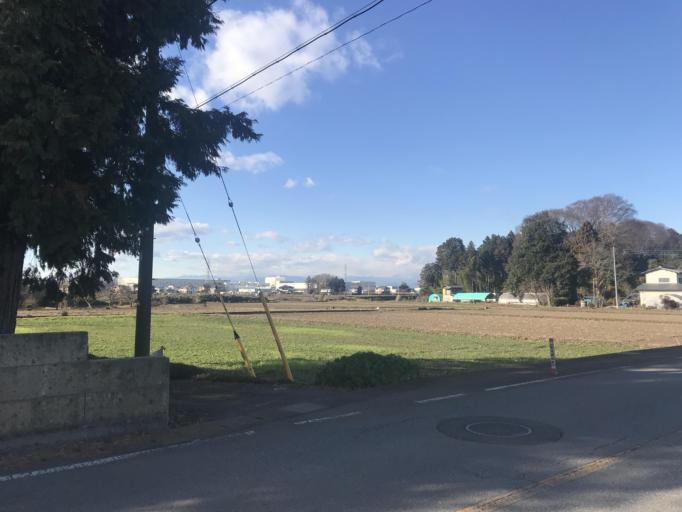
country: JP
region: Tochigi
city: Kaminokawa
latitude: 36.4141
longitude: 139.8776
